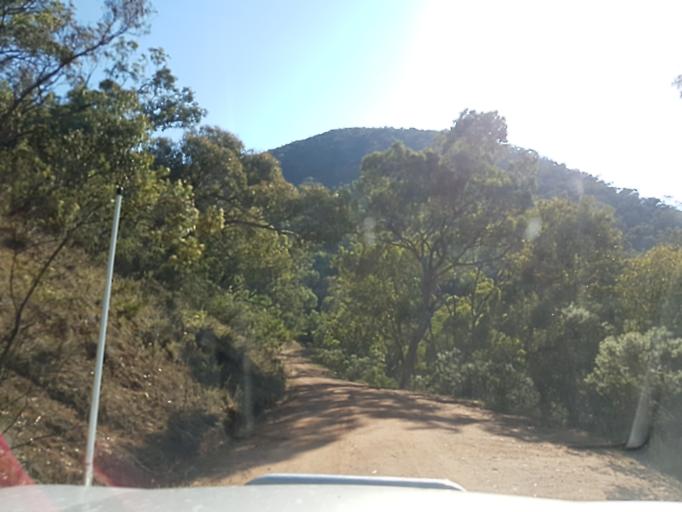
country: AU
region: New South Wales
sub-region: Snowy River
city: Jindabyne
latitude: -36.9320
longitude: 148.3334
